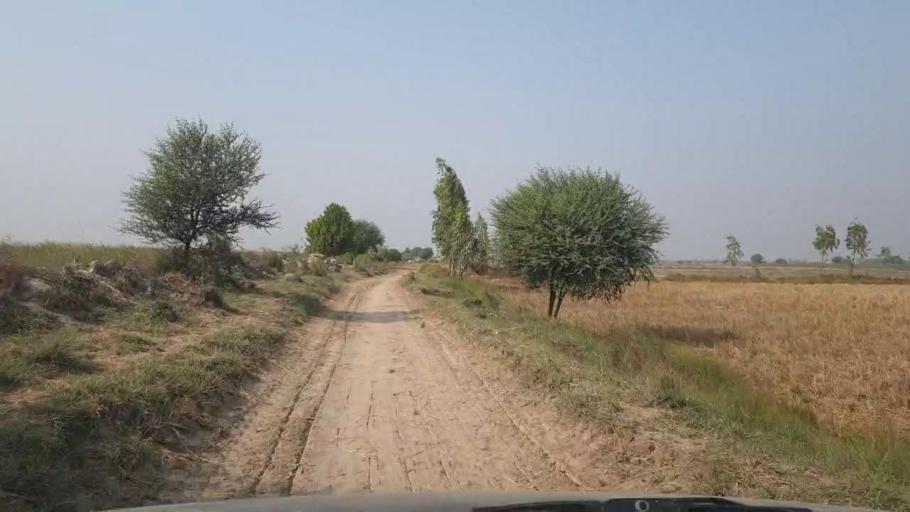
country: PK
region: Sindh
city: Tando Muhammad Khan
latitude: 25.0669
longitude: 68.3587
